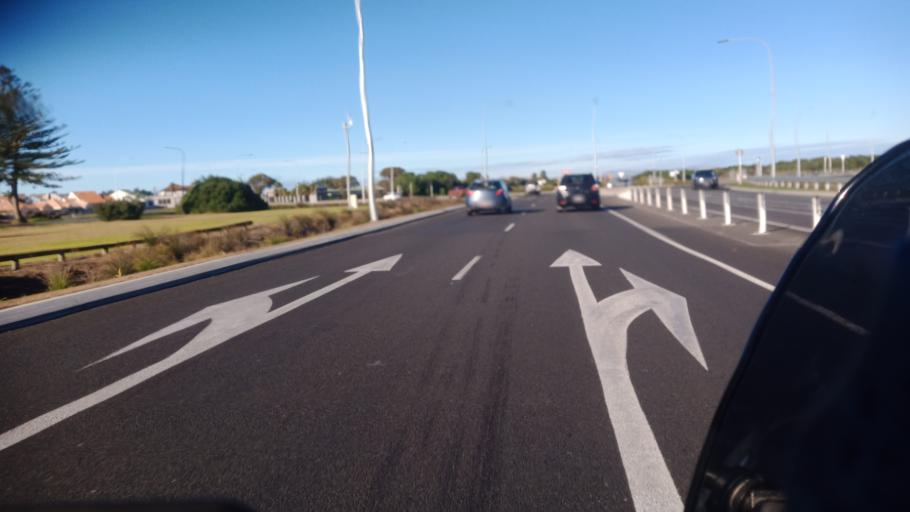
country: NZ
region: Hawke's Bay
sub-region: Napier City
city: Napier
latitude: -39.4735
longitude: 176.8771
